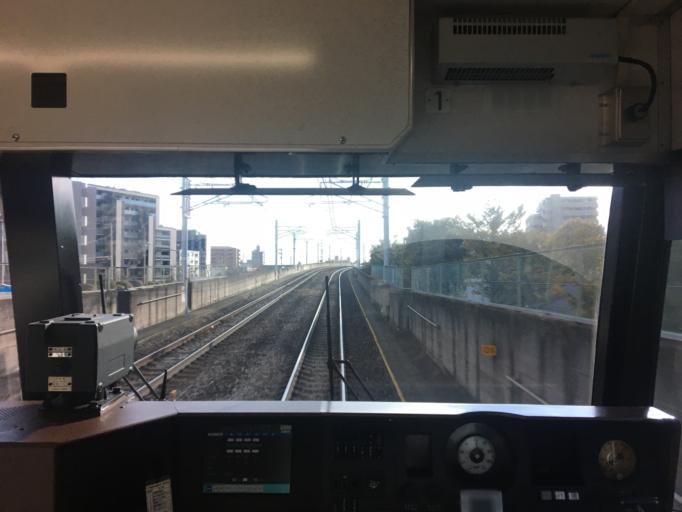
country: JP
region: Miyagi
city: Sendai
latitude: 38.2167
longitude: 140.8710
